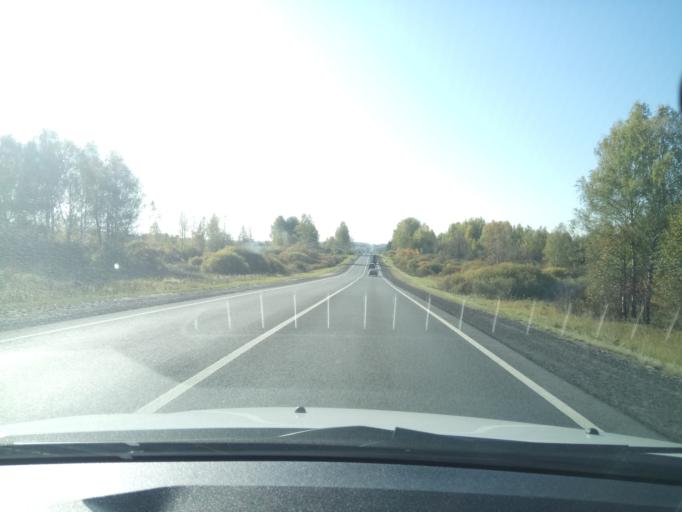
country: RU
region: Nizjnij Novgorod
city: Dal'neye Konstantinovo
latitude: 55.9703
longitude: 43.9736
